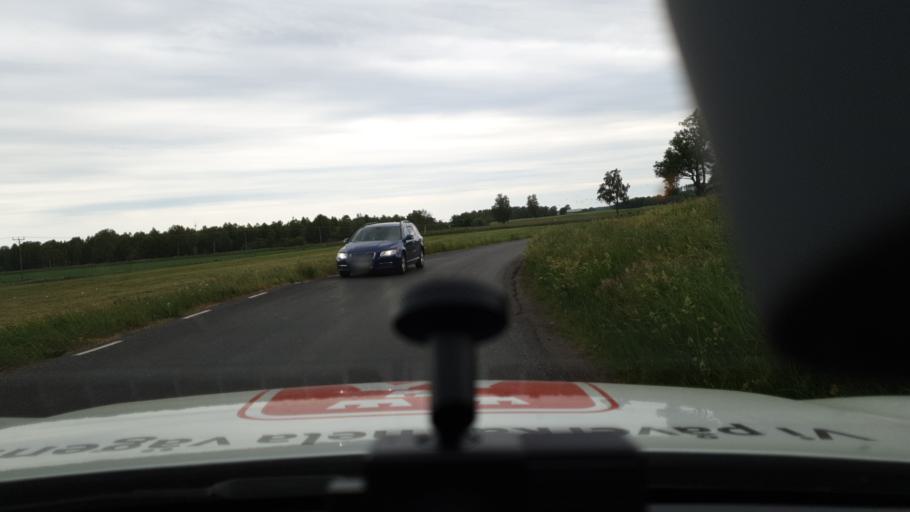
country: SE
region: Vaestra Goetaland
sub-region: Falkopings Kommun
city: Falkoeping
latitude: 58.0993
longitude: 13.4827
